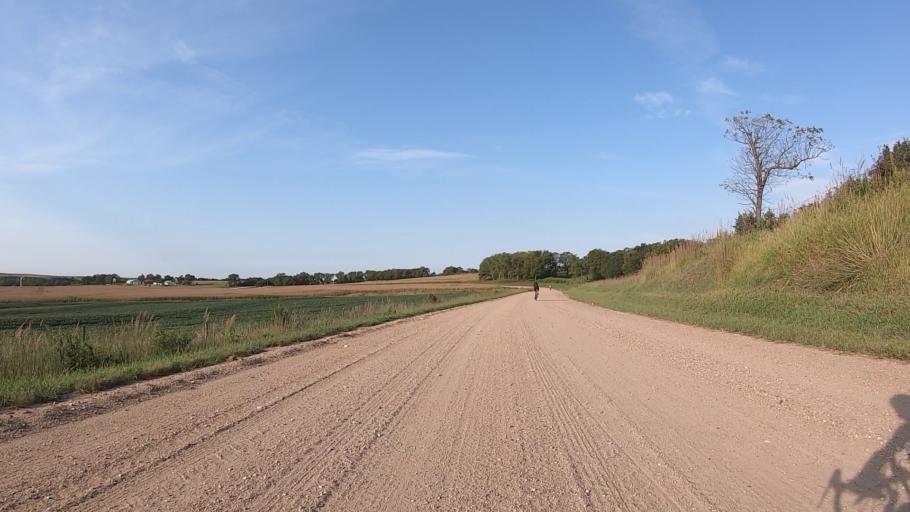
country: US
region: Kansas
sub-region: Marshall County
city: Blue Rapids
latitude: 39.6799
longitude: -96.7818
